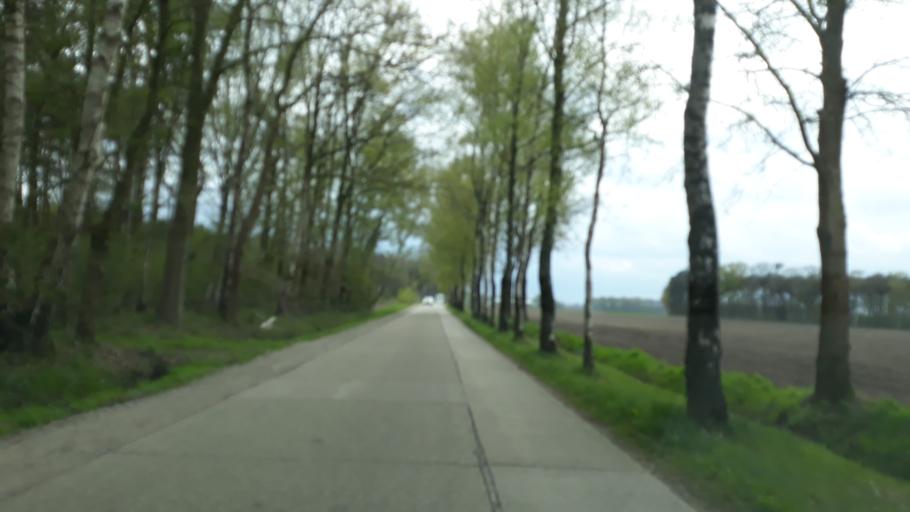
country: BE
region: Flanders
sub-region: Provincie Antwerpen
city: Oud-Turnhout
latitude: 51.2864
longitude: 4.9956
